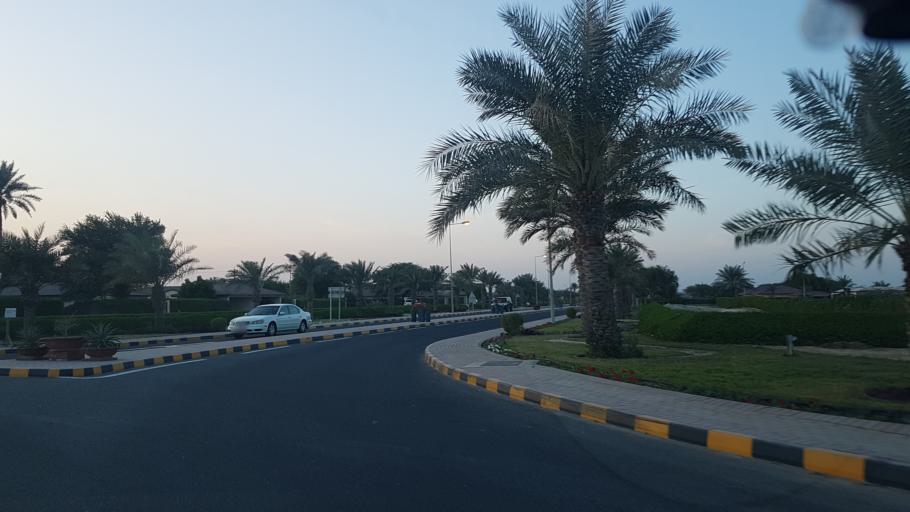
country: BH
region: Northern
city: Ar Rifa'
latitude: 26.0928
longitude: 50.5477
